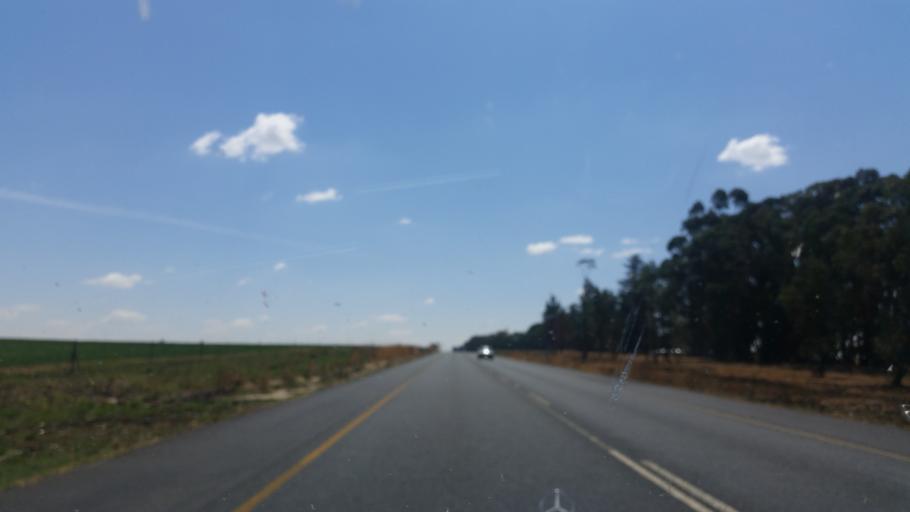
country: ZA
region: Orange Free State
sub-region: Thabo Mofutsanyana District Municipality
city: Bethlehem
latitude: -28.0979
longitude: 28.6570
